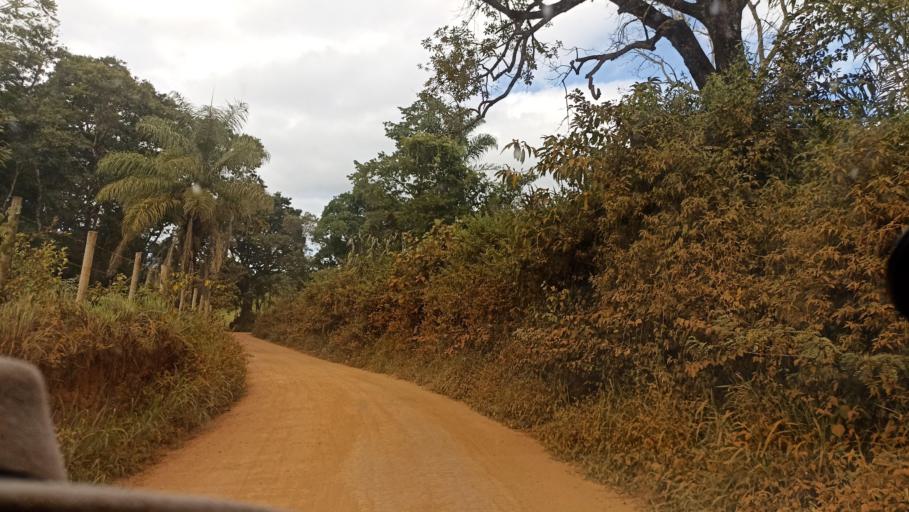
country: BR
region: Minas Gerais
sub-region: Tiradentes
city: Tiradentes
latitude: -21.1032
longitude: -44.1097
